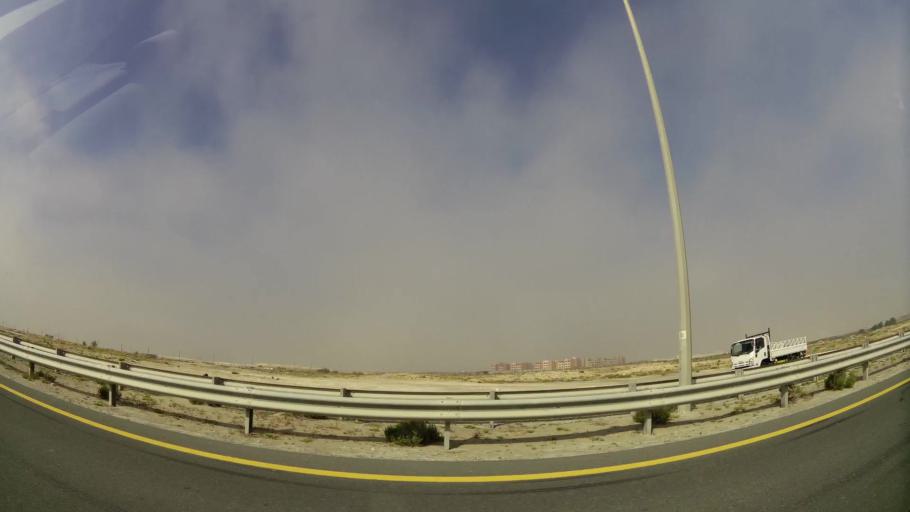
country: AE
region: Dubai
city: Dubai
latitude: 24.9532
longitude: 55.0560
